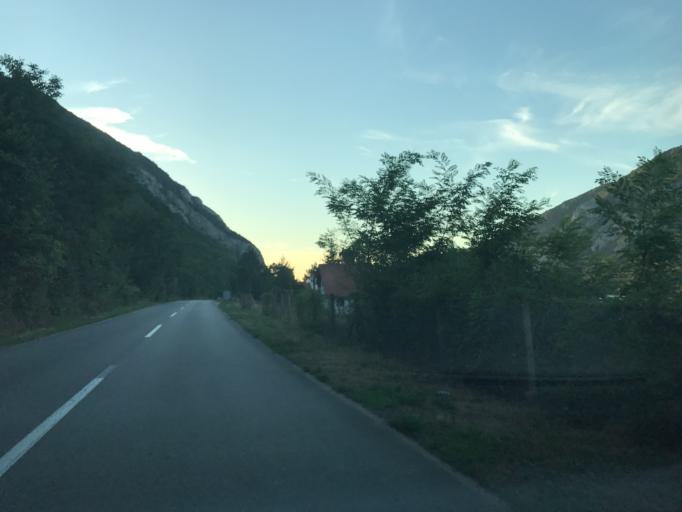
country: RO
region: Caras-Severin
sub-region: Comuna Pescari
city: Coronini
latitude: 44.6544
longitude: 21.7098
